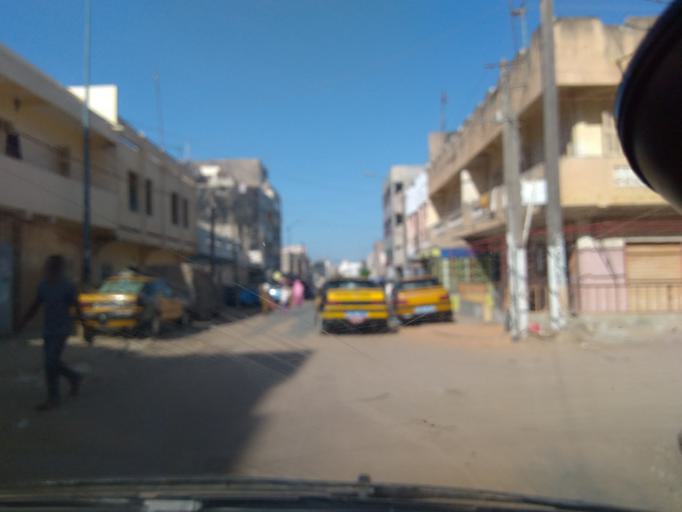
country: SN
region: Dakar
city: Pikine
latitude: 14.7561
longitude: -17.4344
